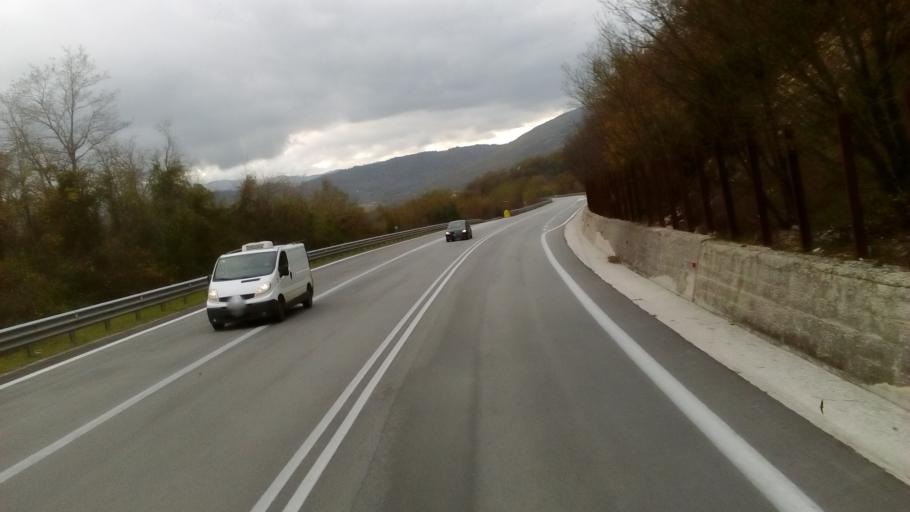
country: IT
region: Molise
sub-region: Provincia di Isernia
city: Sessano del Molise
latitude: 41.6474
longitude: 14.3308
